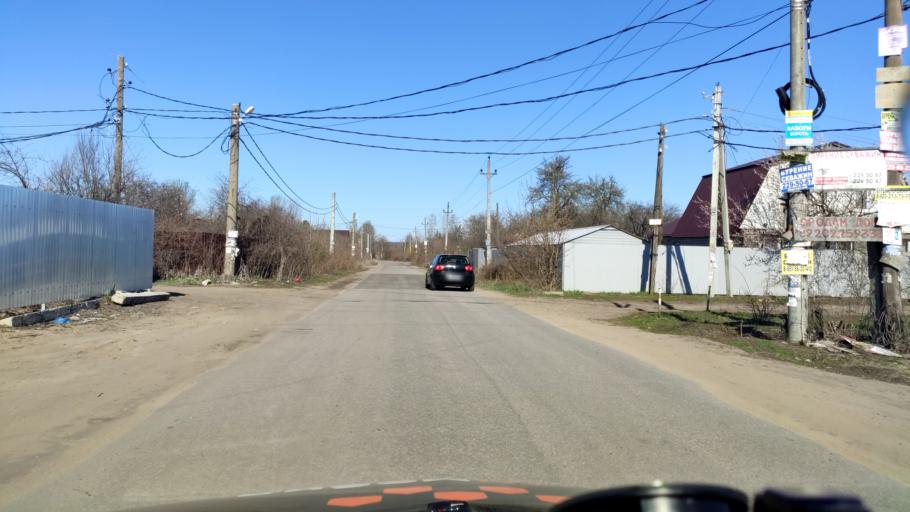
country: RU
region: Voronezj
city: Maslovka
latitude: 51.5871
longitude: 39.1670
